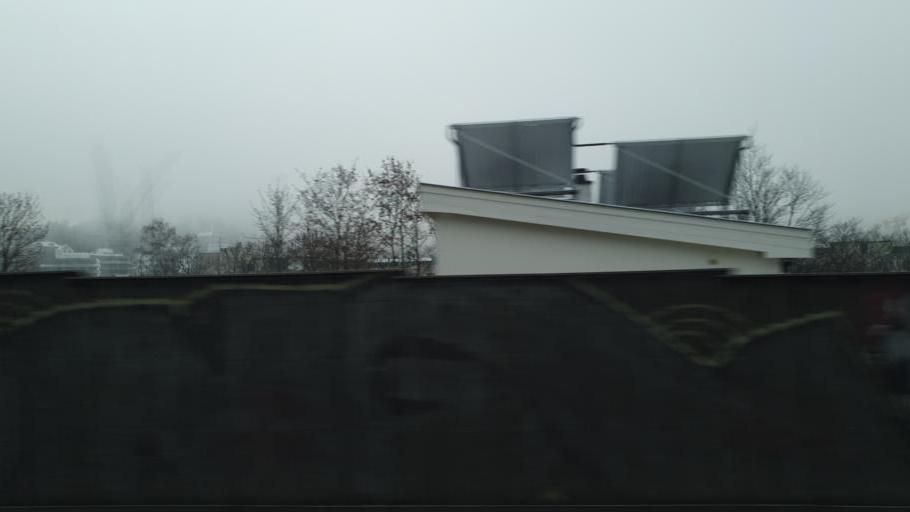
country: NO
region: Akershus
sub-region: Lorenskog
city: Kjenn
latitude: 59.9317
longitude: 10.9221
